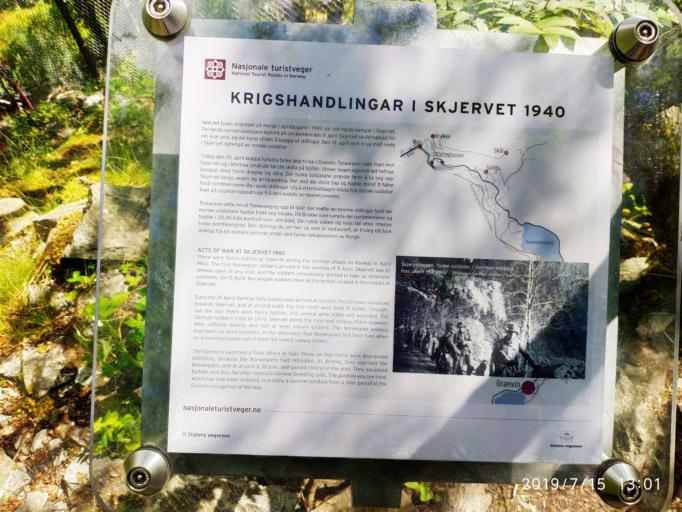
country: NO
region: Hordaland
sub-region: Granvin
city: Granvin
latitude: 60.5877
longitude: 6.6356
